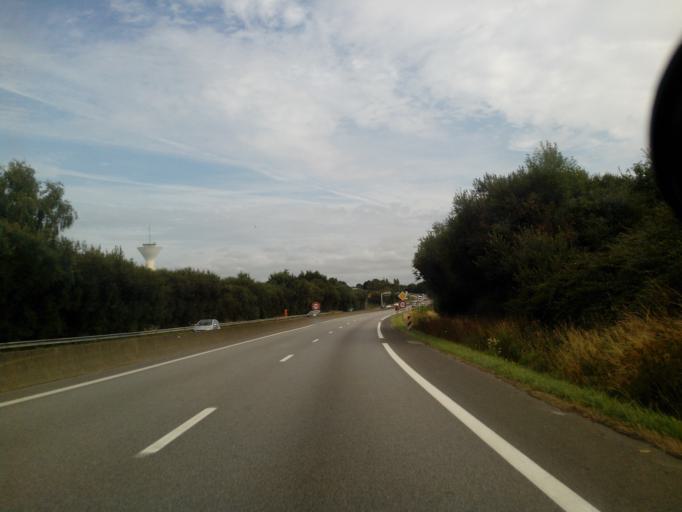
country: FR
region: Brittany
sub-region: Departement du Morbihan
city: Sene
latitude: 47.6500
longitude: -2.7040
